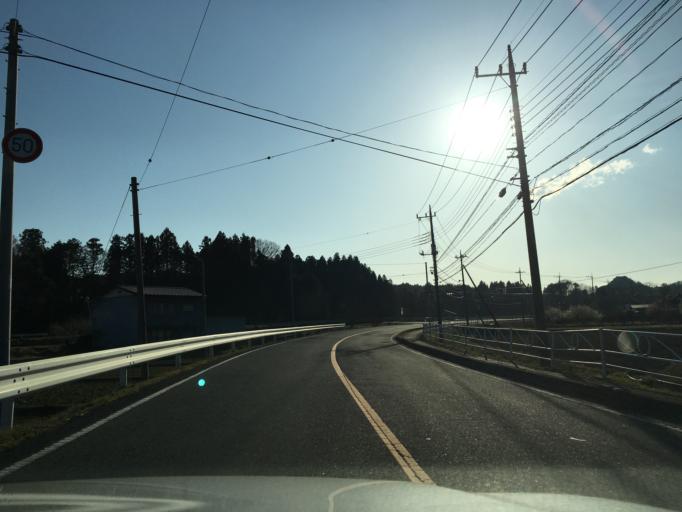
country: JP
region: Ibaraki
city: Daigo
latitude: 36.7782
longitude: 140.3046
